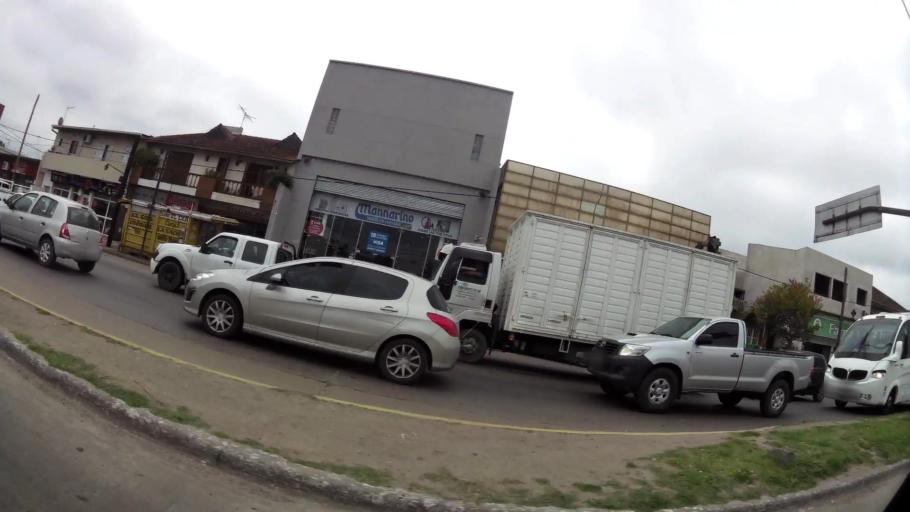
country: AR
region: Buenos Aires
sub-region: Partido de La Plata
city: La Plata
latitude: -34.9950
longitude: -58.0478
